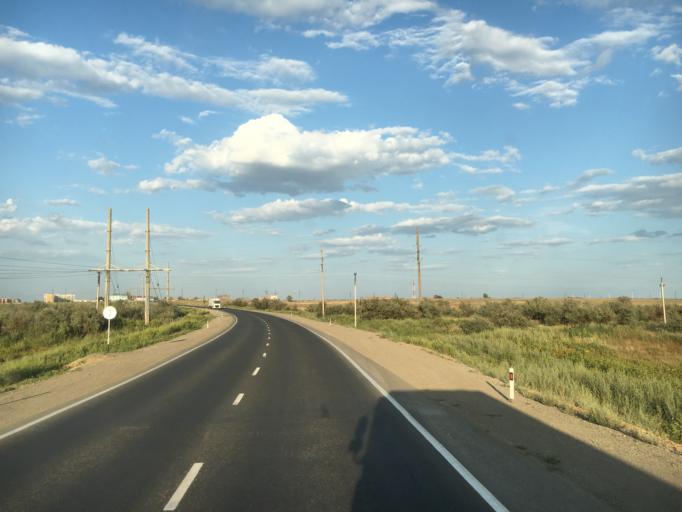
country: KZ
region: Aqtoebe
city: Aqtobe
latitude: 50.2713
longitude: 57.1075
